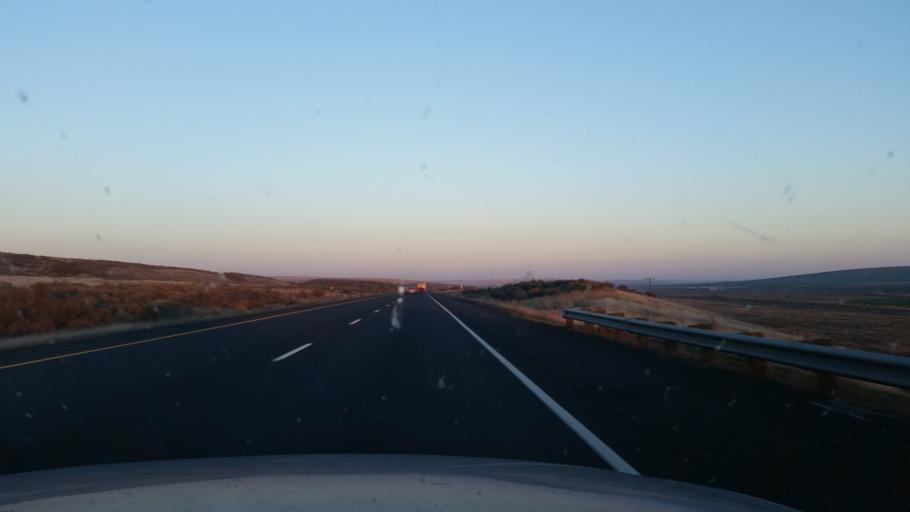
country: US
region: Washington
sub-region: Grant County
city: Warden
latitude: 47.0858
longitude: -118.9391
